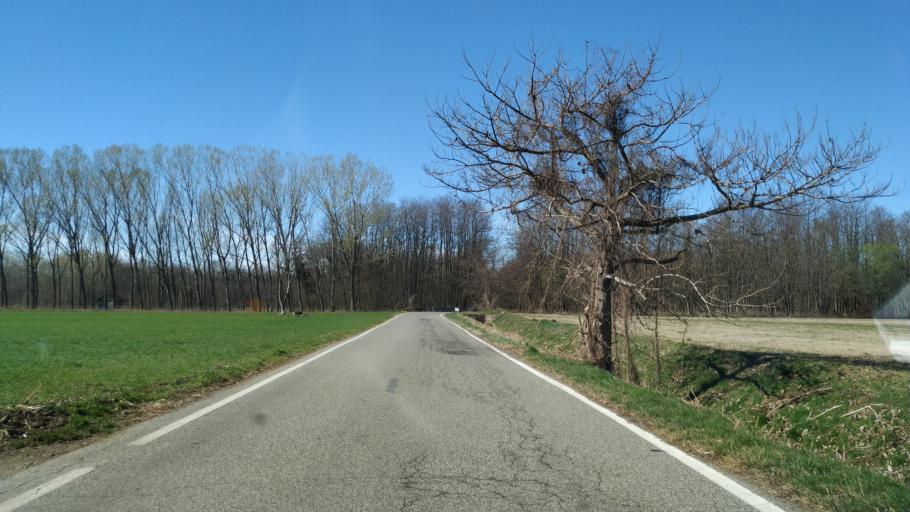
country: IT
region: Piedmont
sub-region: Provincia di Novara
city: Ghemme
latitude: 45.5878
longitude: 8.4183
